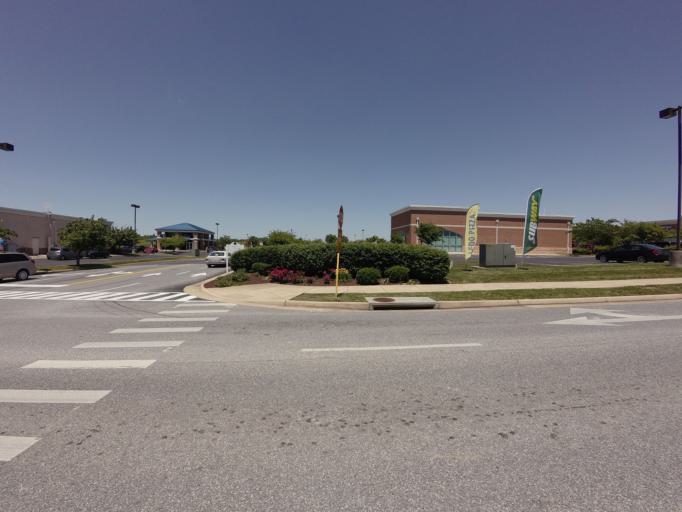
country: US
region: West Virginia
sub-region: Jefferson County
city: Ranson
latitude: 39.3202
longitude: -77.8485
